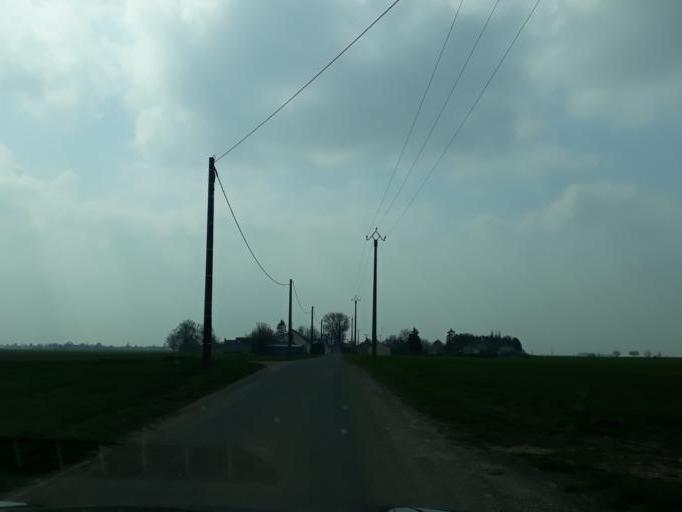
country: FR
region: Centre
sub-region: Departement d'Eure-et-Loir
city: Baigneaux
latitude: 48.0693
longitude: 1.7985
